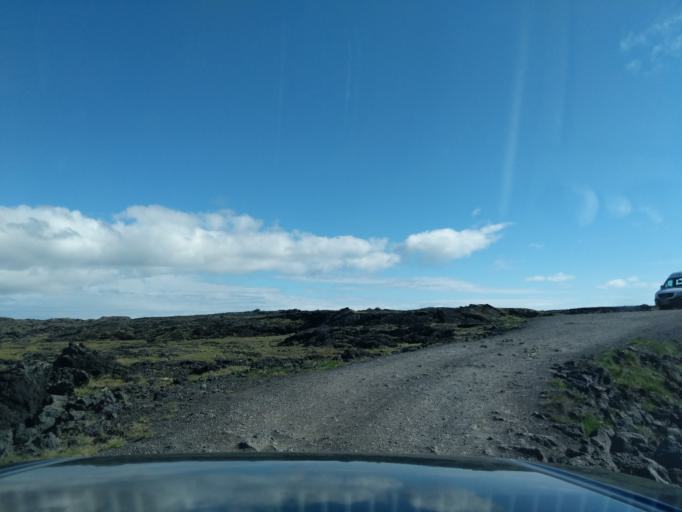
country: IS
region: West
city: Olafsvik
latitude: 64.8643
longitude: -24.0383
